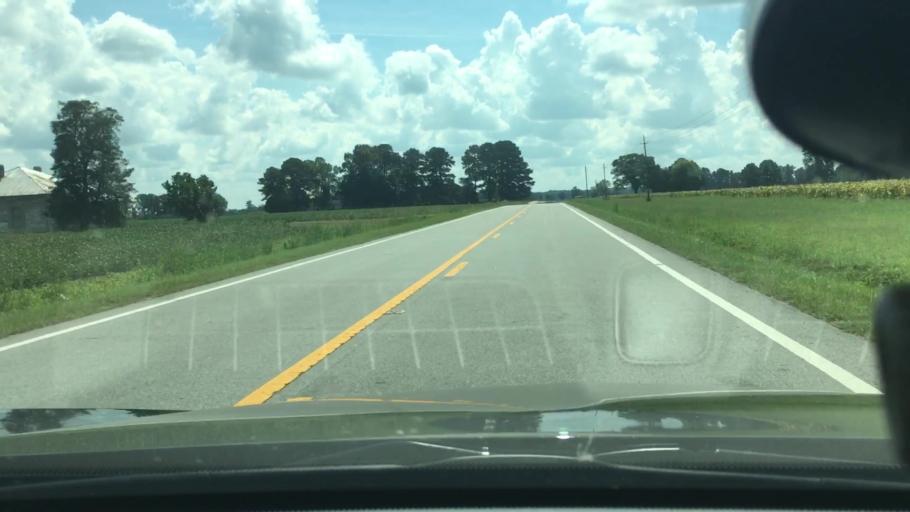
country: US
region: North Carolina
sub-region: Pitt County
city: Farmville
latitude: 35.6709
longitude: -77.4827
